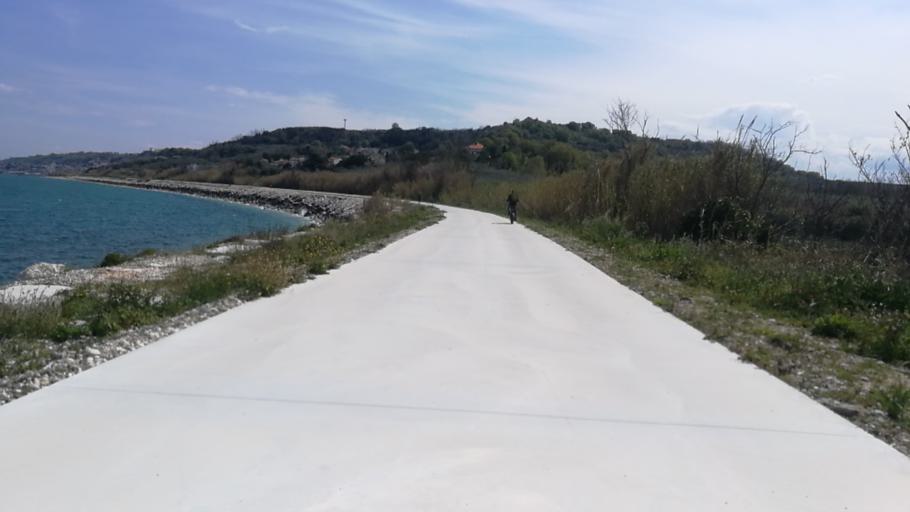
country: IT
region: Abruzzo
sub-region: Provincia di Chieti
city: Marina di San Vito
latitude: 42.3279
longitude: 14.4247
